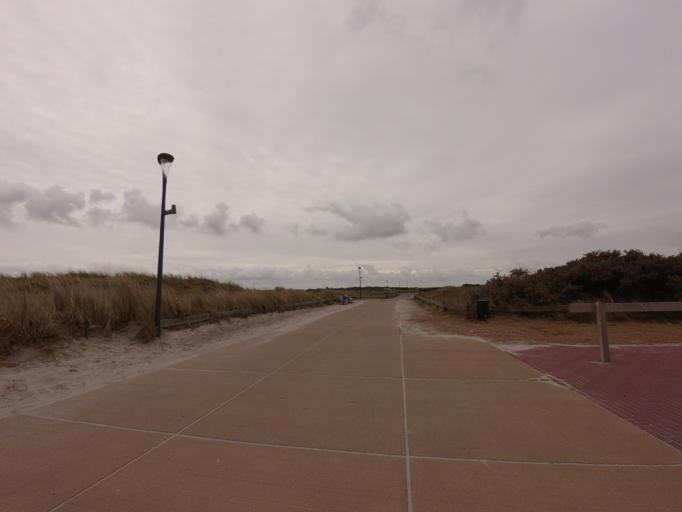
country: NL
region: Friesland
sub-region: Gemeente Ameland
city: Hollum
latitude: 53.4592
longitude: 5.6856
